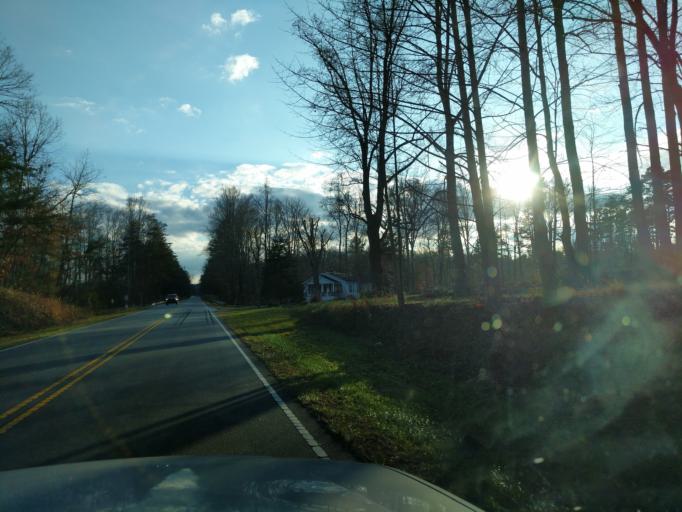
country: US
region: North Carolina
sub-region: Rutherford County
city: Rutherfordton
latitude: 35.5111
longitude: -81.9735
